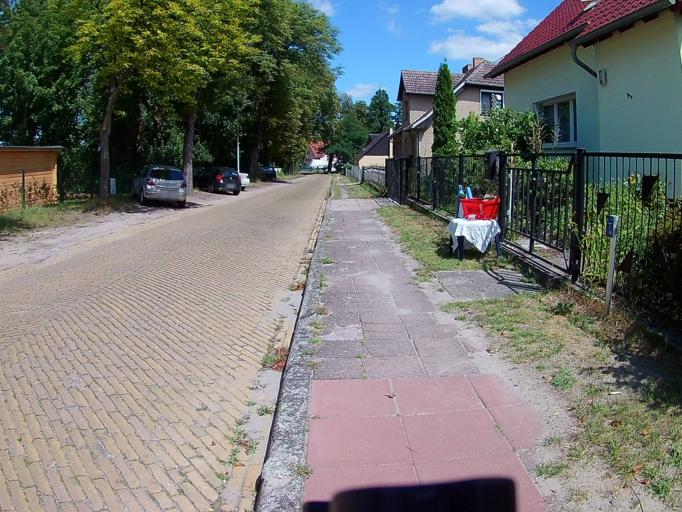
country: DE
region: Brandenburg
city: Gross Koris
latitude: 52.1630
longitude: 13.6568
